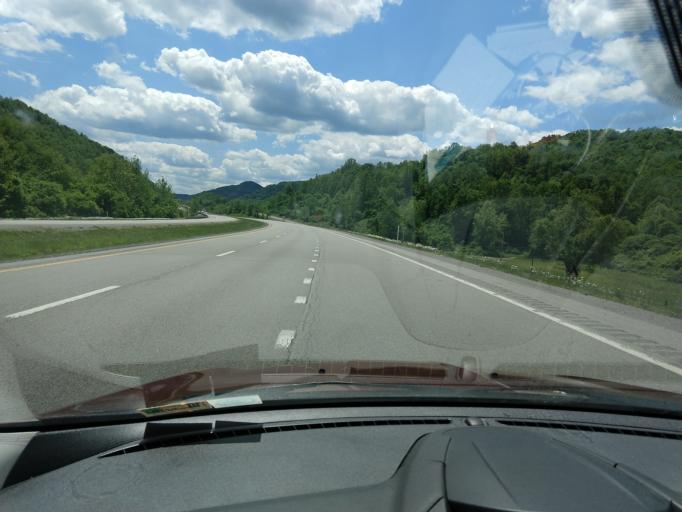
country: US
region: West Virginia
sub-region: Gilmer County
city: Glenville
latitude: 38.8544
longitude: -80.6629
